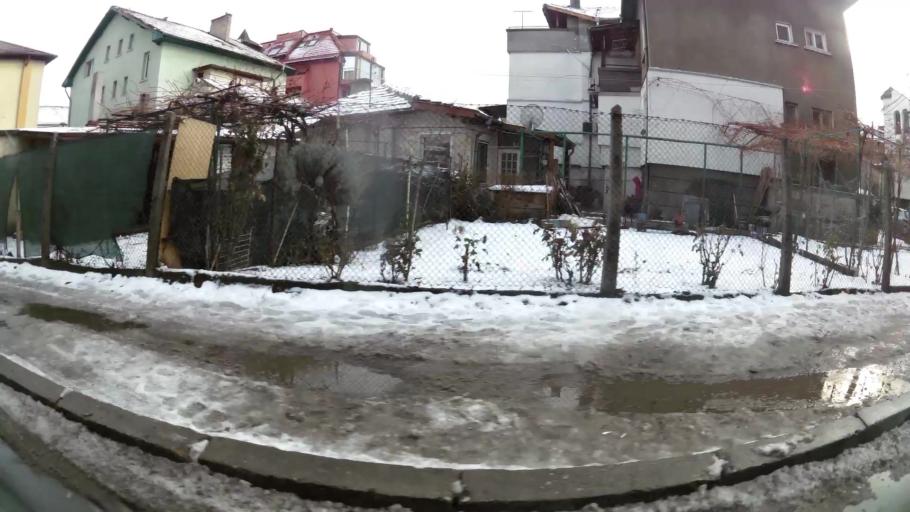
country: BG
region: Sofia-Capital
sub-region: Stolichna Obshtina
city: Sofia
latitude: 42.6988
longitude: 23.3673
